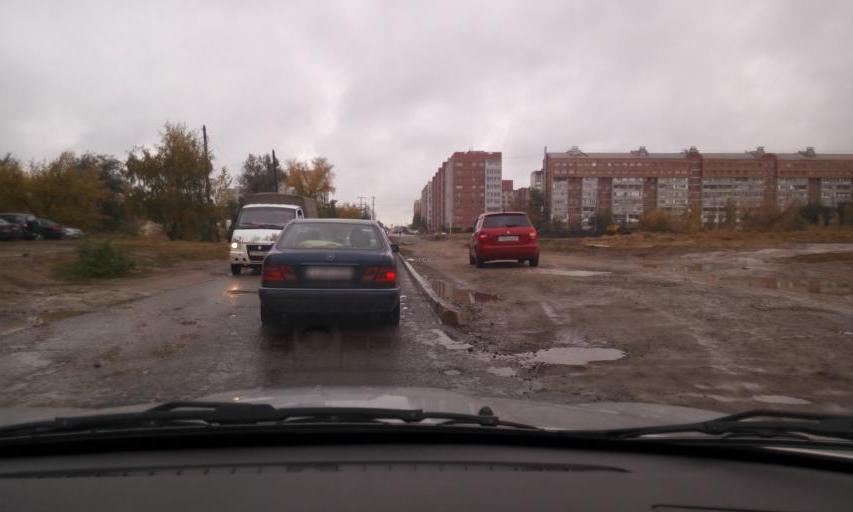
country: KZ
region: Astana Qalasy
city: Astana
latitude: 51.1629
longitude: 71.4007
